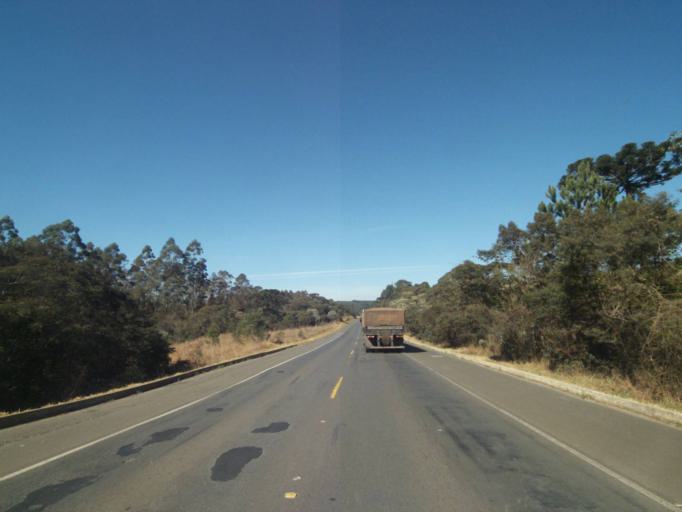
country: BR
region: Parana
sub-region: Tibagi
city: Tibagi
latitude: -24.5694
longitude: -50.4524
